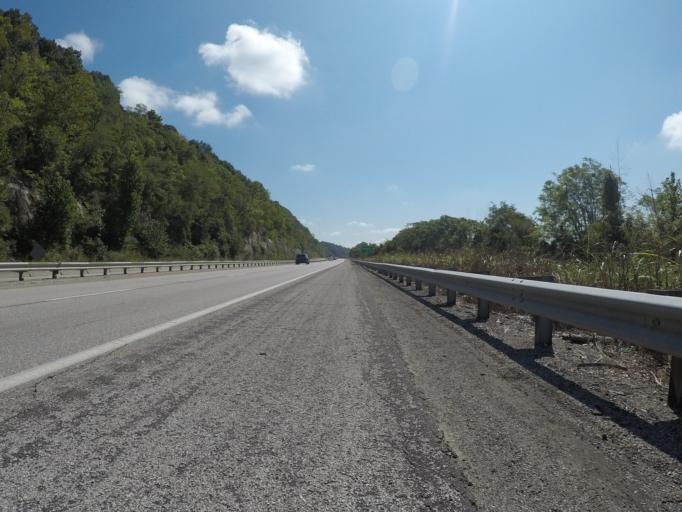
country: US
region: Kentucky
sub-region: Boyd County
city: Ashland
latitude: 38.4764
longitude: -82.6152
